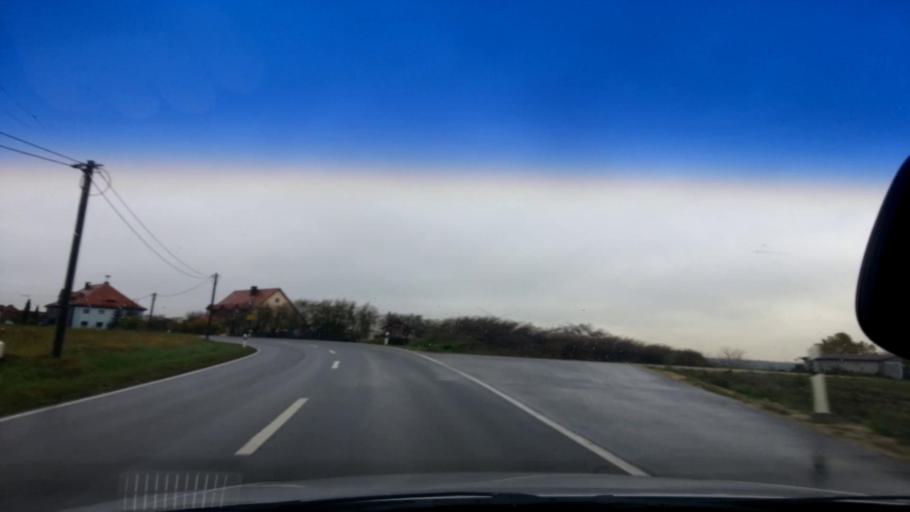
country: DE
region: Bavaria
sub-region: Upper Franconia
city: Wattendorf
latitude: 50.0013
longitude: 11.1352
